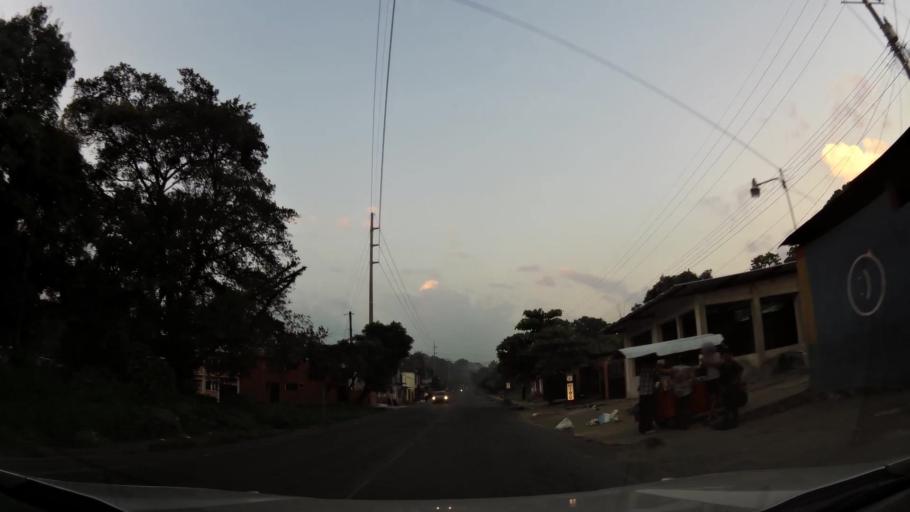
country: GT
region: Retalhuleu
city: Santa Cruz Mulua
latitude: 14.5859
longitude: -91.6221
